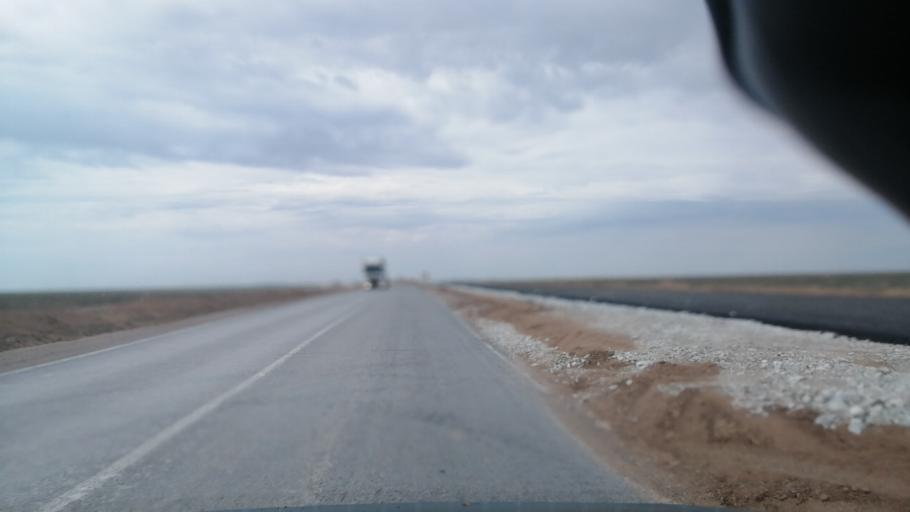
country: KZ
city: Priozersk
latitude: 46.5499
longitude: 74.1800
